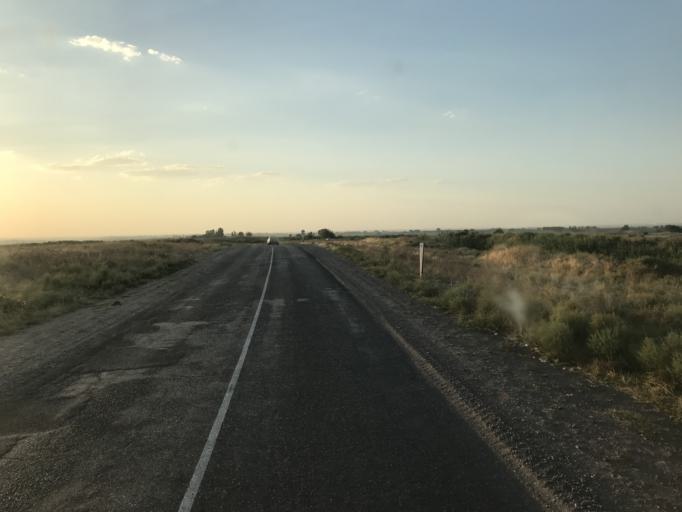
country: UZ
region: Toshkent
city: Yangiyul
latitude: 41.3410
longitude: 68.8784
